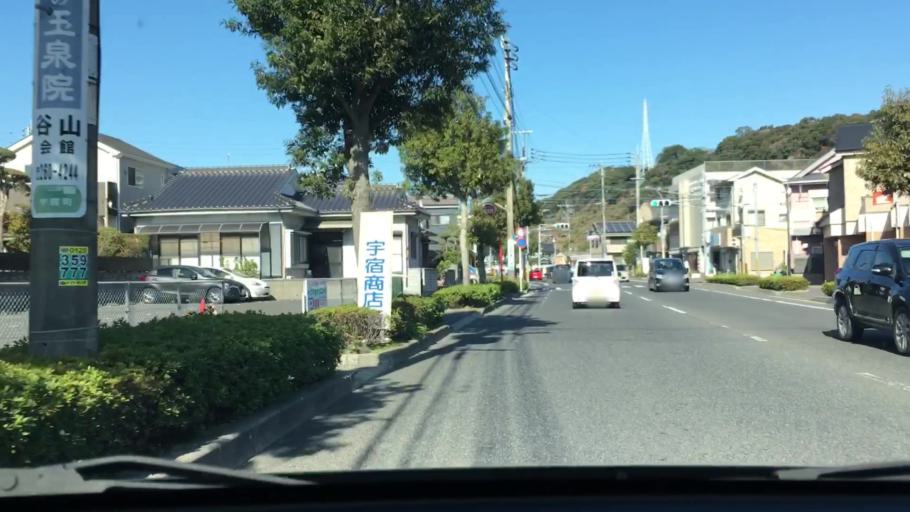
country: JP
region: Kagoshima
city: Kagoshima-shi
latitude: 31.5471
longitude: 130.5333
